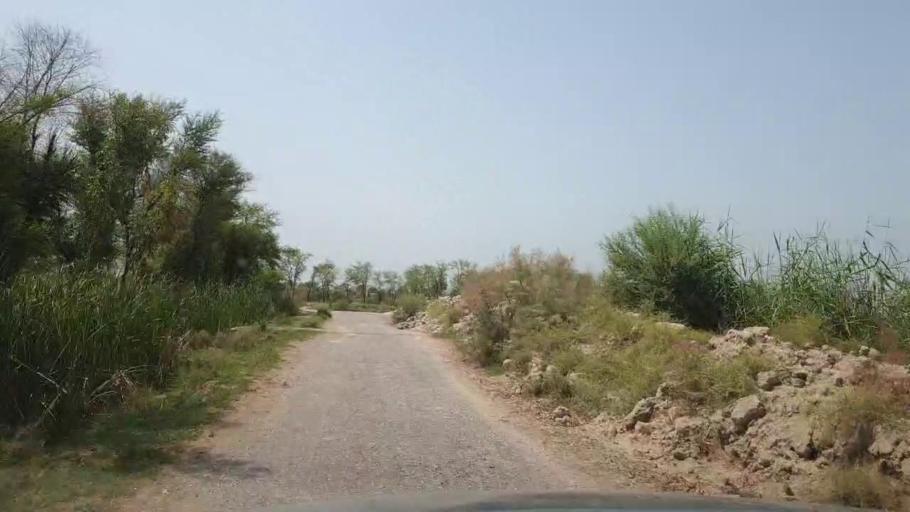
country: PK
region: Sindh
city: Garhi Yasin
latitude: 27.8941
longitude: 68.4522
